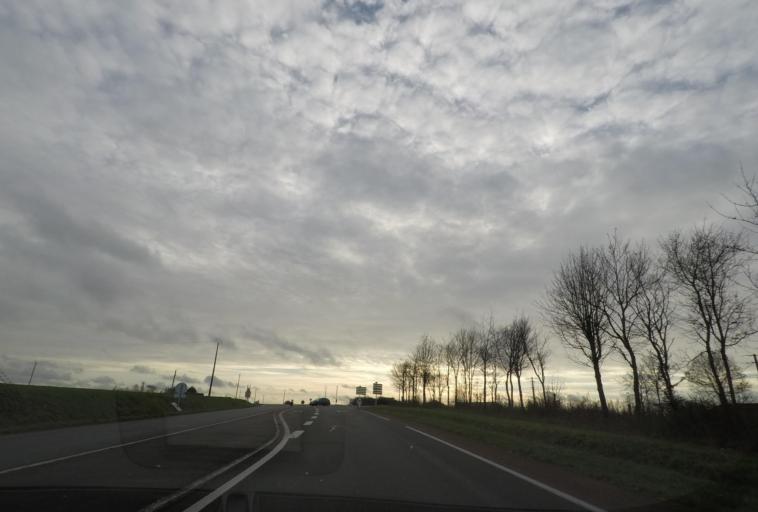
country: FR
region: Pays de la Loire
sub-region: Departement de la Sarthe
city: Saint-Calais
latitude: 47.9196
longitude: 0.7652
